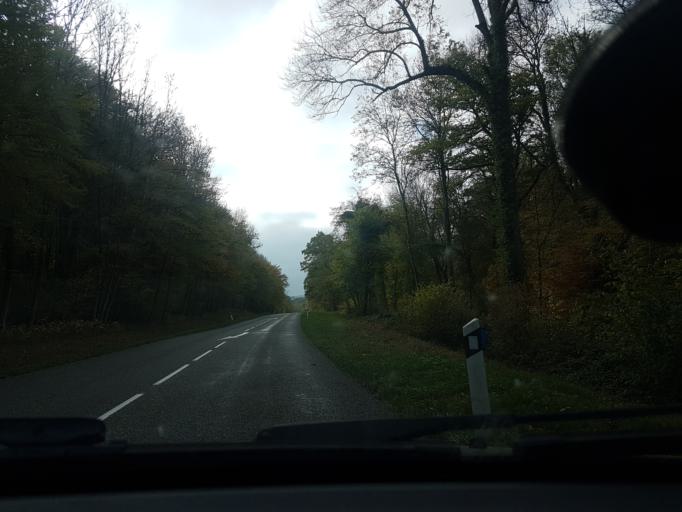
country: FR
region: Franche-Comte
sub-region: Territoire de Belfort
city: Essert
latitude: 47.6462
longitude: 6.8102
